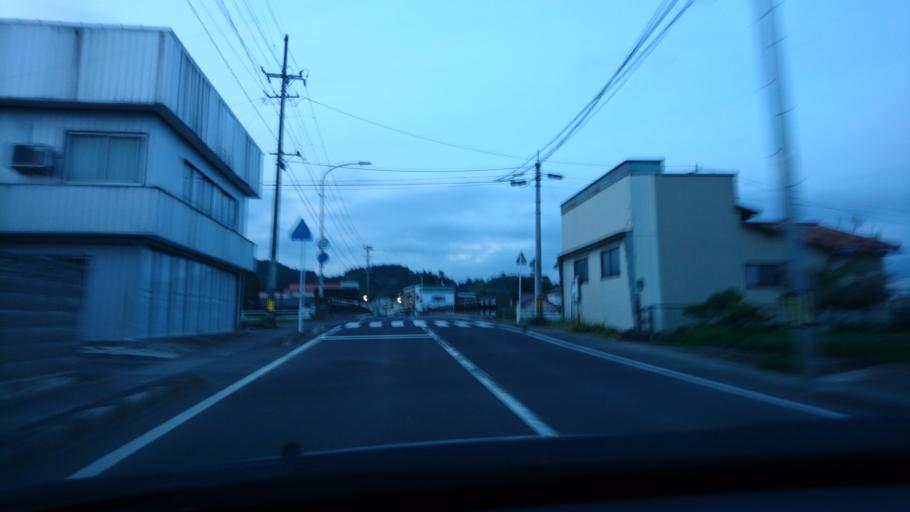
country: JP
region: Iwate
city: Ichinoseki
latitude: 38.8276
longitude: 140.9858
